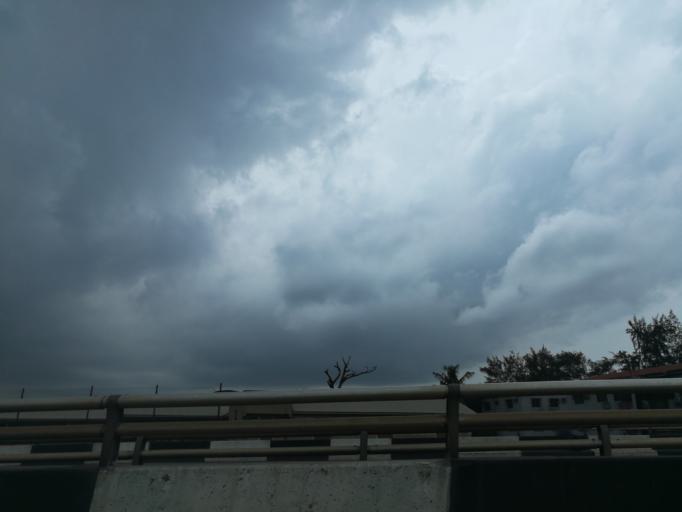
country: NG
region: Lagos
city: Lagos
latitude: 6.4527
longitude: 3.4084
